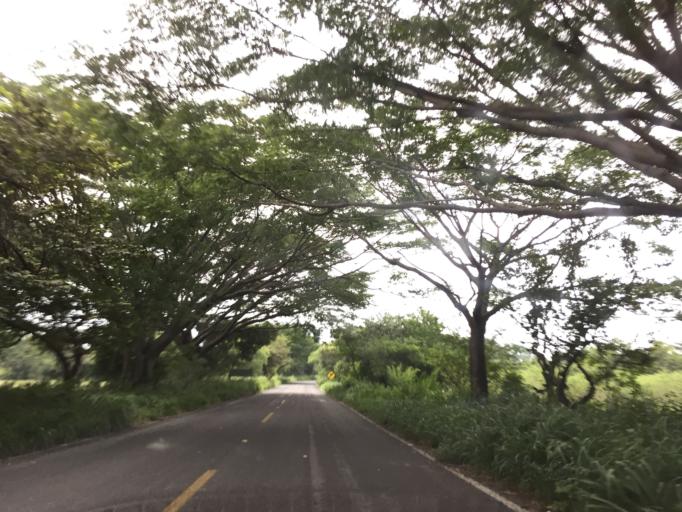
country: MX
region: Colima
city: Comala
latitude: 19.3483
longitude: -103.7876
